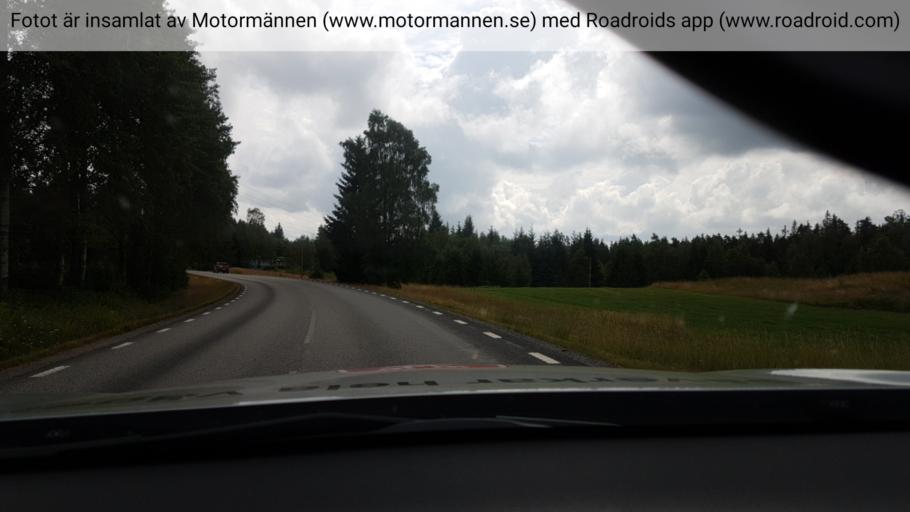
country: SE
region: Vaestra Goetaland
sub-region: Svenljunga Kommun
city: Svenljunga
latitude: 57.4865
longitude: 13.1352
